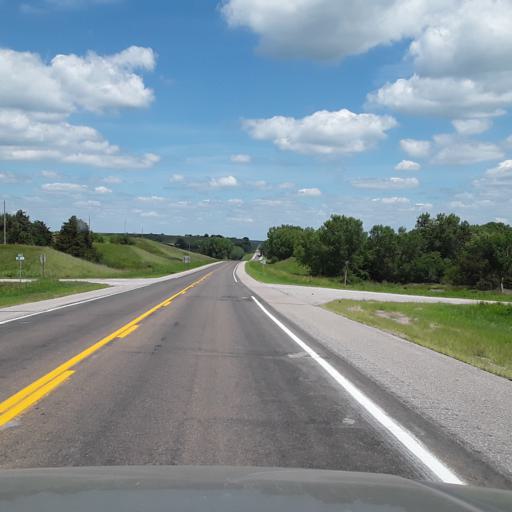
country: US
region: Nebraska
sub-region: Nance County
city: Genoa
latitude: 41.4685
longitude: -97.7163
